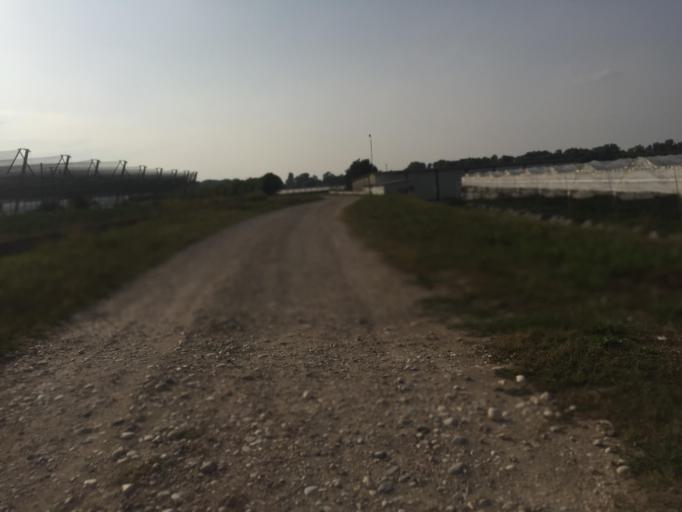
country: IT
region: Veneto
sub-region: Provincia di Verona
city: Campagnola
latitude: 45.3820
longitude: 11.0825
